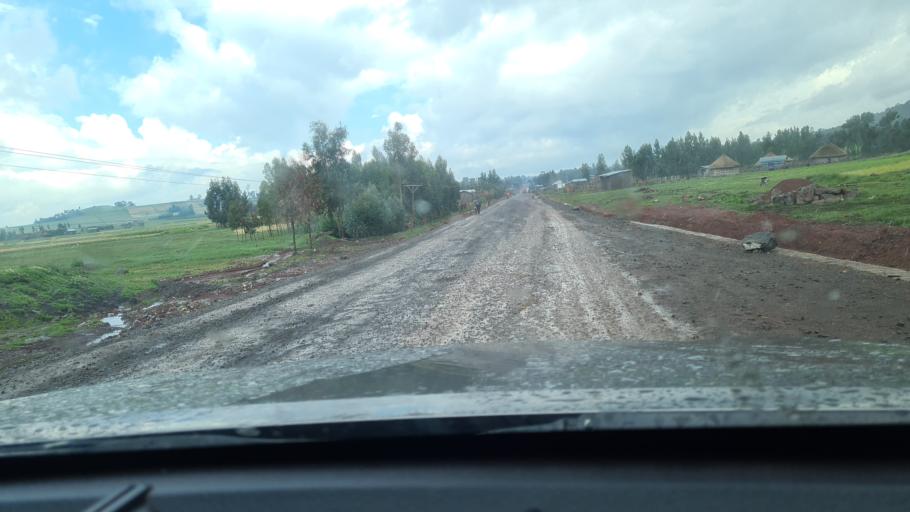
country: ET
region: Oromiya
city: Huruta
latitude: 8.0780
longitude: 39.5461
